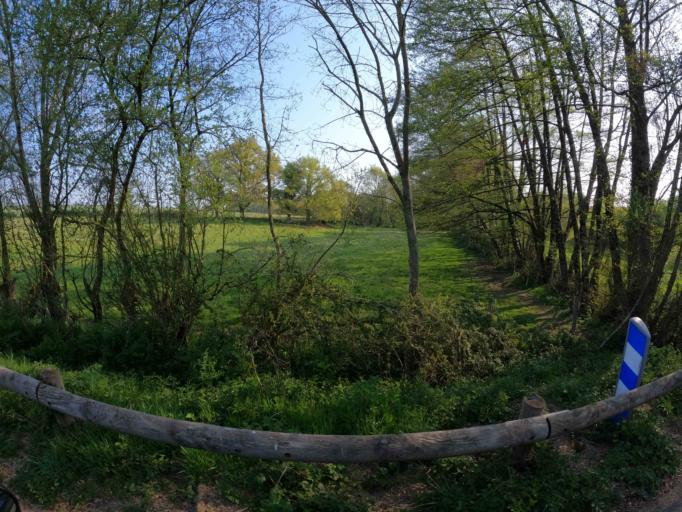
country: FR
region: Pays de la Loire
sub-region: Departement de Maine-et-Loire
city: La Seguiniere
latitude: 47.0682
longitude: -0.9601
